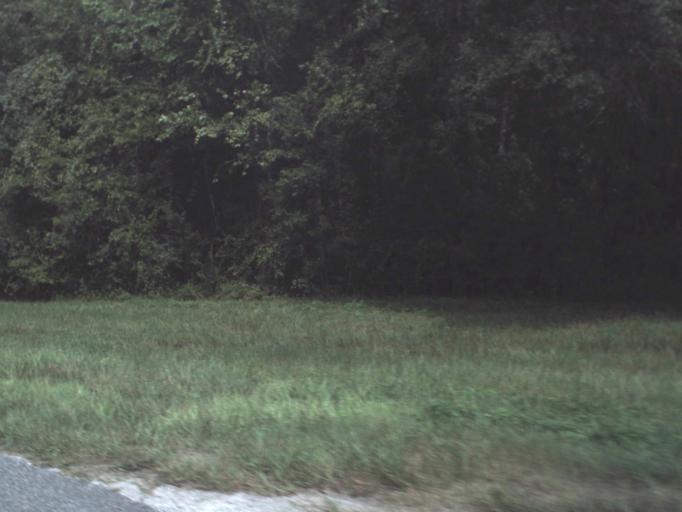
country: US
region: Florida
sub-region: Hernando County
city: Ridge Manor
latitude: 28.5220
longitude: -82.0988
